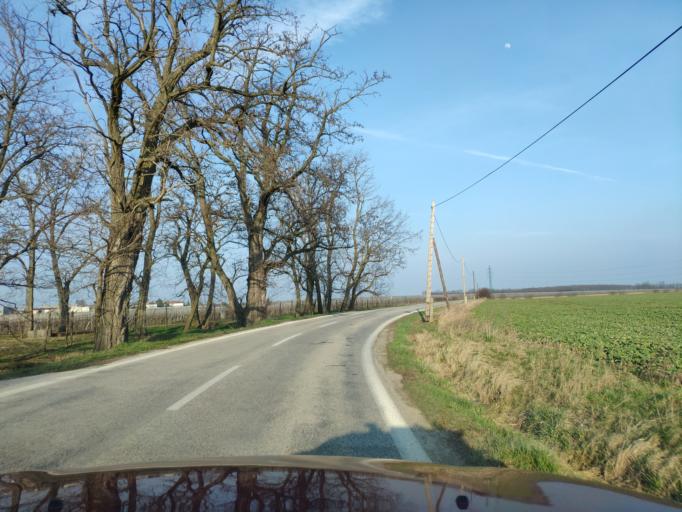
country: SK
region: Bratislavsky
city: Modra
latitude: 48.3166
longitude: 17.3690
